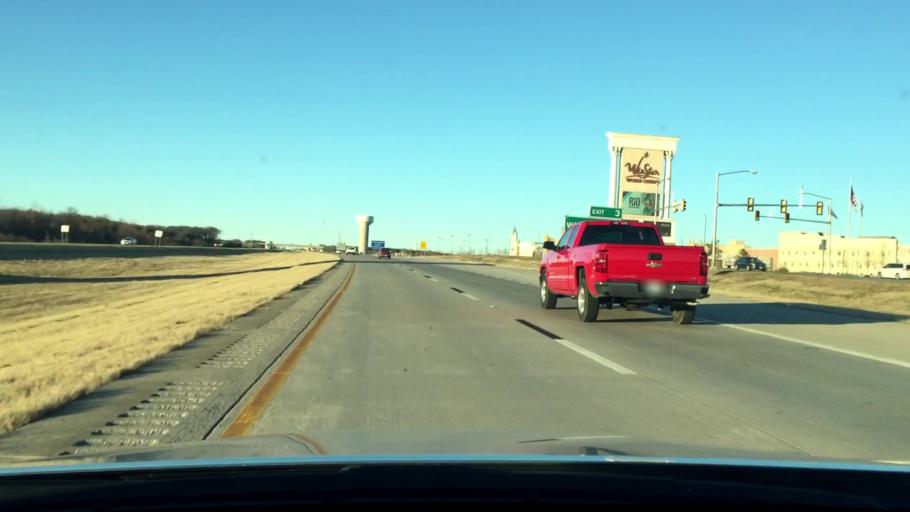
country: US
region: Texas
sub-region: Cooke County
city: Gainesville
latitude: 33.7547
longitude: -97.1349
